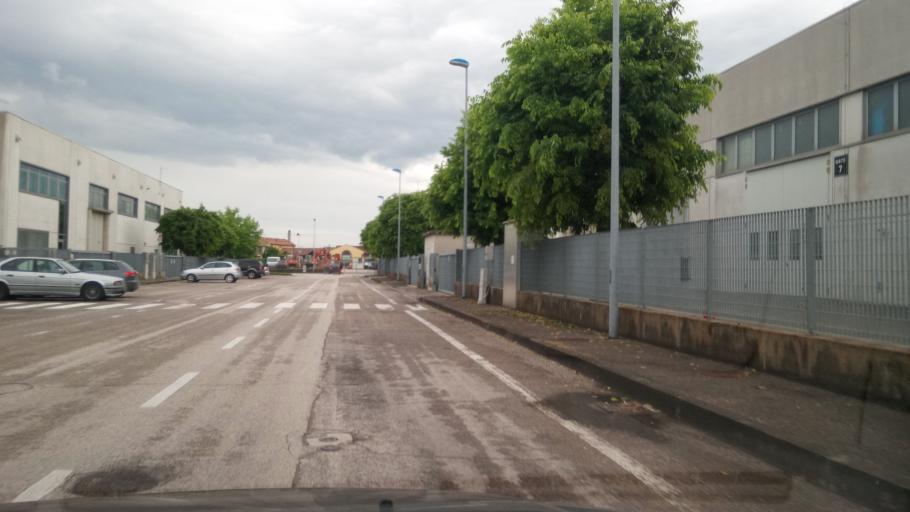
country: IT
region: Veneto
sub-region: Provincia di Padova
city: Mestrino
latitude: 45.4469
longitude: 11.7472
